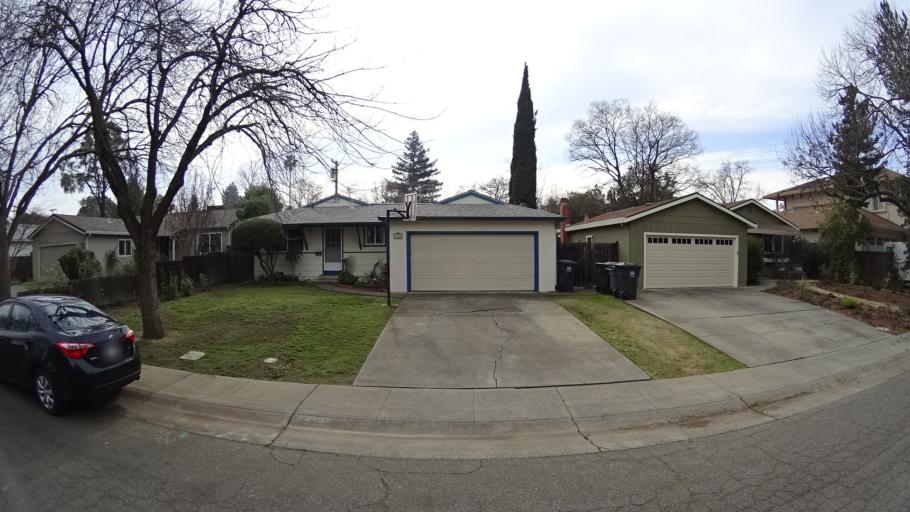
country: US
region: California
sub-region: Yolo County
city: Davis
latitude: 38.5581
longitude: -121.7337
